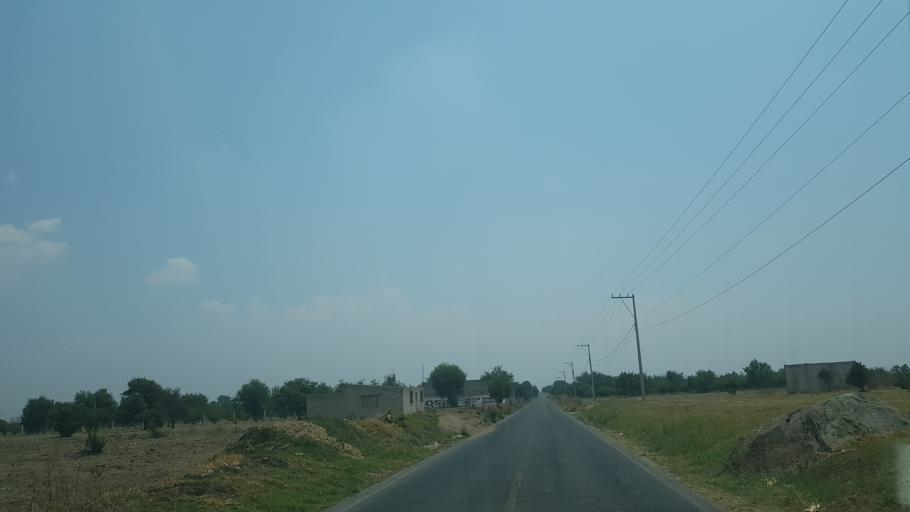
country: MX
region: Puebla
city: San Andres Calpan
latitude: 19.0992
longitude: -98.4320
